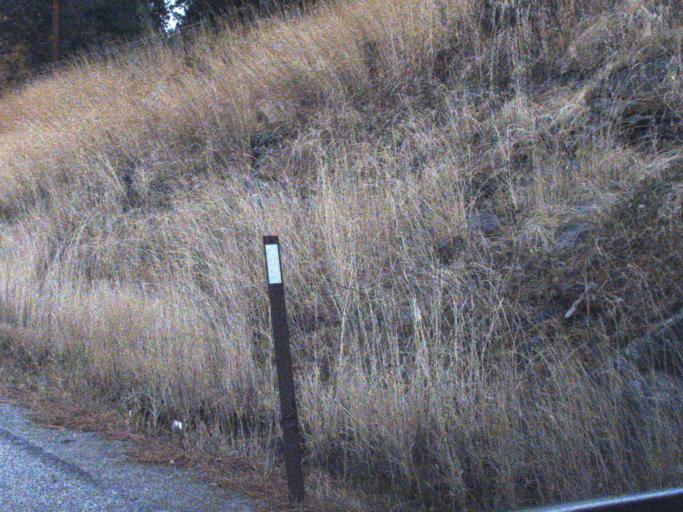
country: US
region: Washington
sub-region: Stevens County
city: Kettle Falls
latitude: 48.6562
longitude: -118.1137
